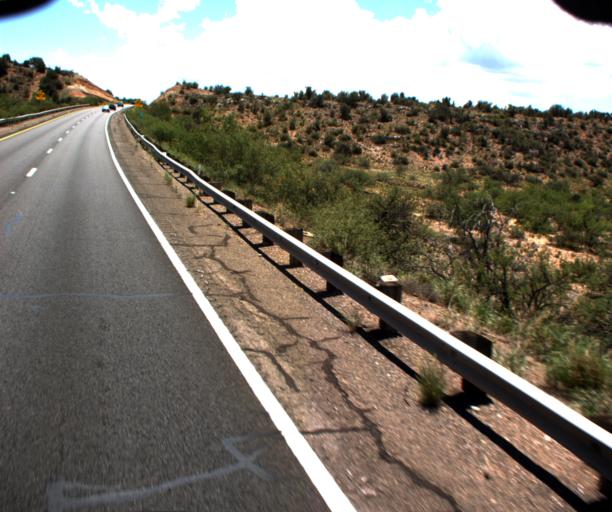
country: US
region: Arizona
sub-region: Yavapai County
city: Verde Village
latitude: 34.6772
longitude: -111.9728
